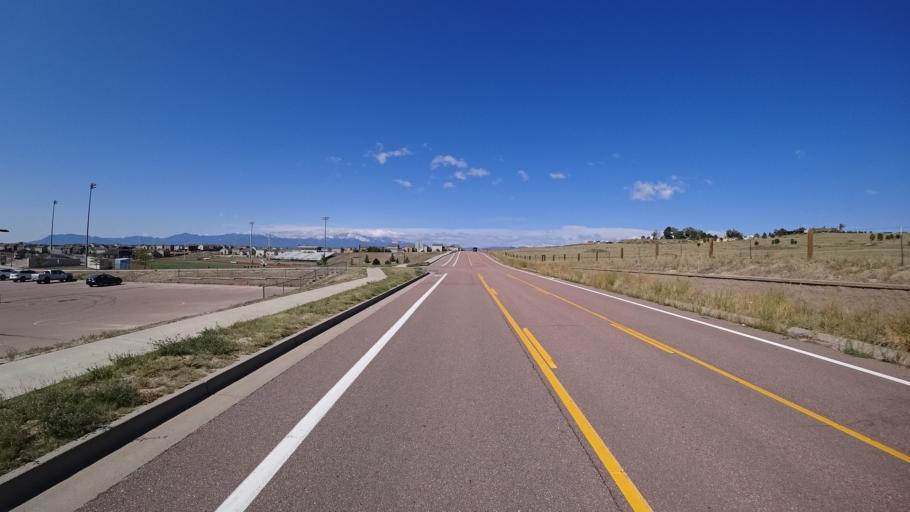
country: US
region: Colorado
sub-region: El Paso County
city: Cimarron Hills
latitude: 38.9335
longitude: -104.7034
